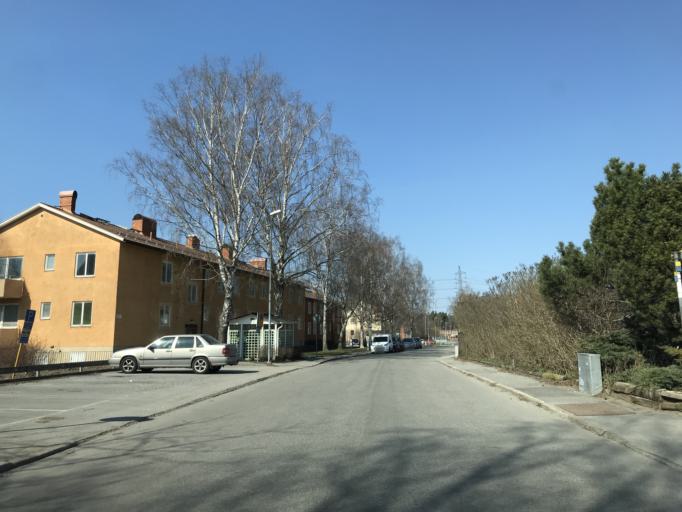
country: SE
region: Stockholm
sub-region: Sollentuna Kommun
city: Sollentuna
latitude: 59.4418
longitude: 17.9405
